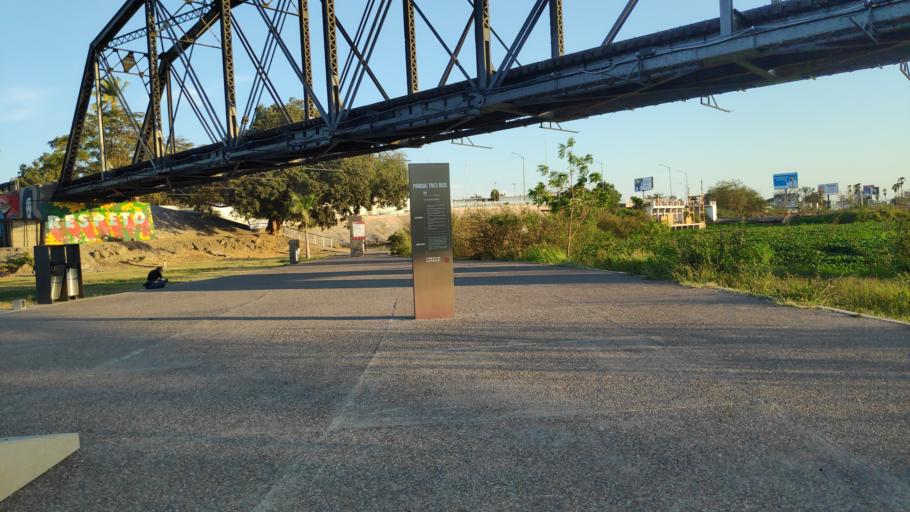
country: MX
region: Sinaloa
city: Culiacan
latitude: 24.8079
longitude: -107.4085
